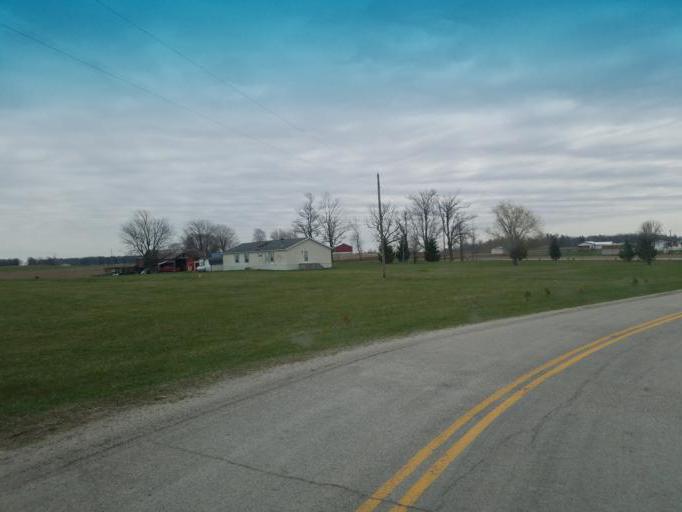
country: US
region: Ohio
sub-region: Crawford County
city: Bucyrus
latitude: 40.8561
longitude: -82.9307
